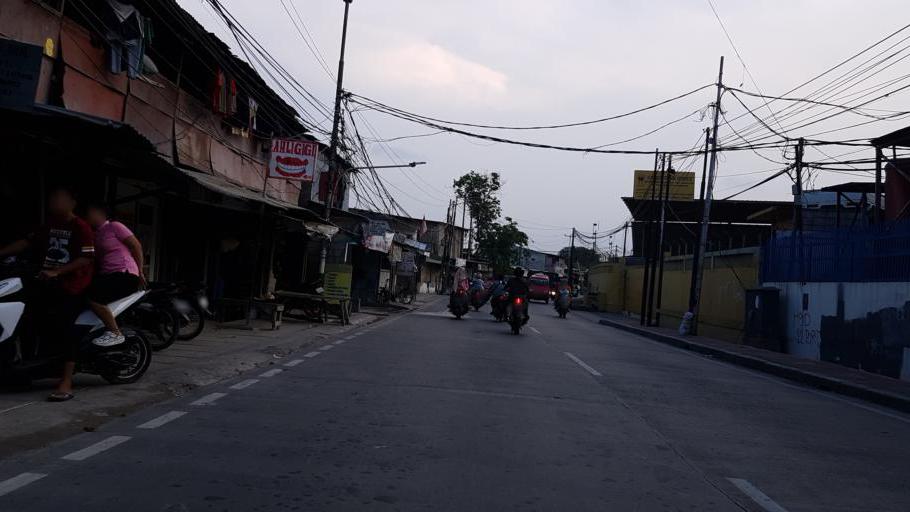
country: ID
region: Jakarta Raya
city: Jakarta
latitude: -6.1398
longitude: 106.7754
